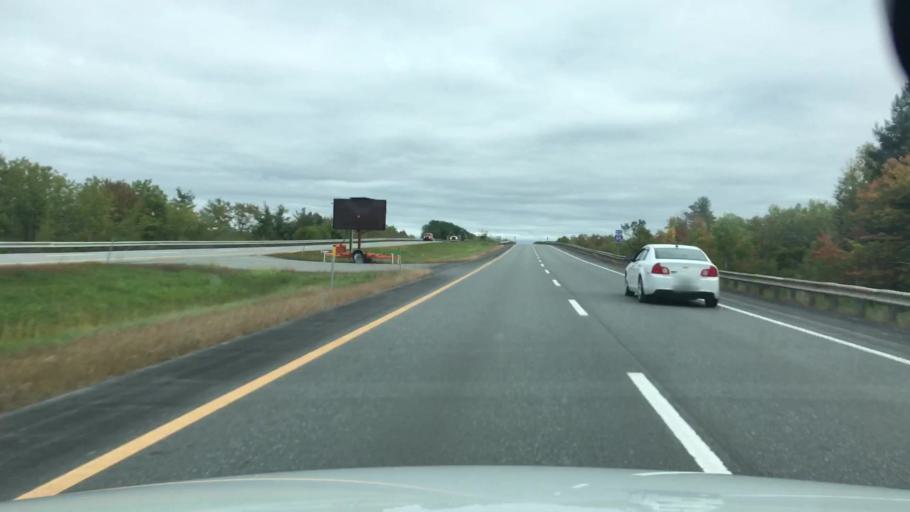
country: US
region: Maine
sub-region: Penobscot County
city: Newport
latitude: 44.8308
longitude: -69.2855
